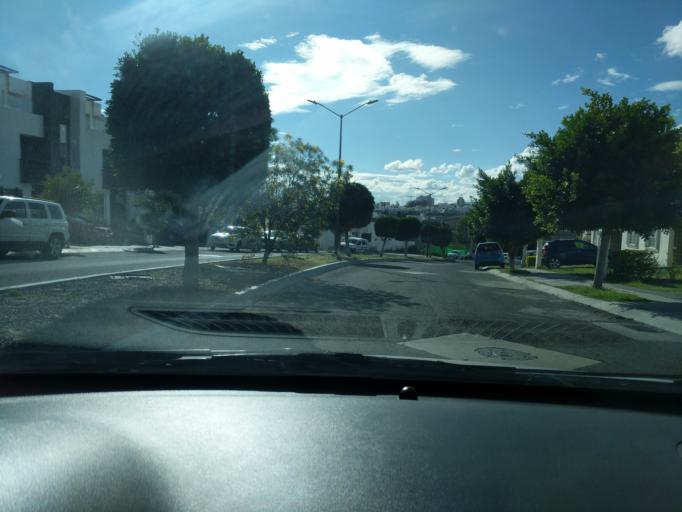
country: MX
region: Queretaro
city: La Canada
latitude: 20.5854
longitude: -100.3376
